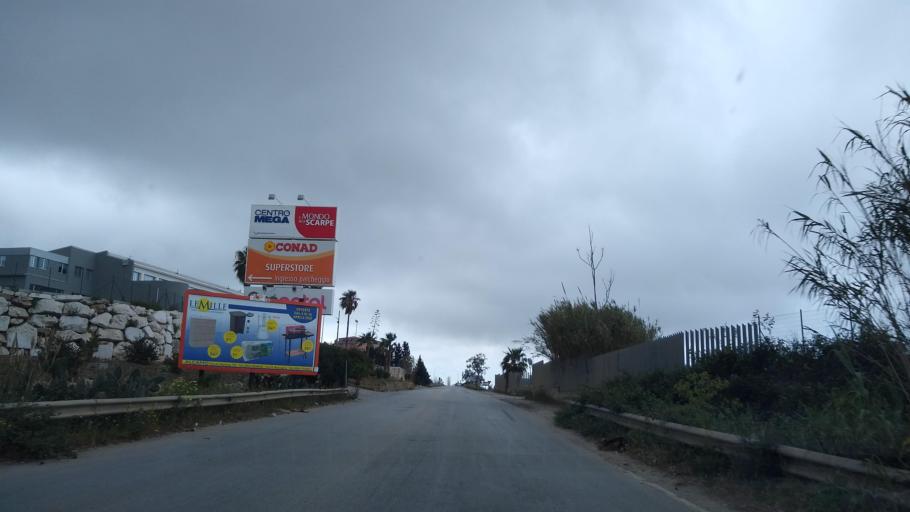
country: IT
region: Sicily
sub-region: Trapani
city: Alcamo
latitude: 37.9833
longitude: 12.9501
